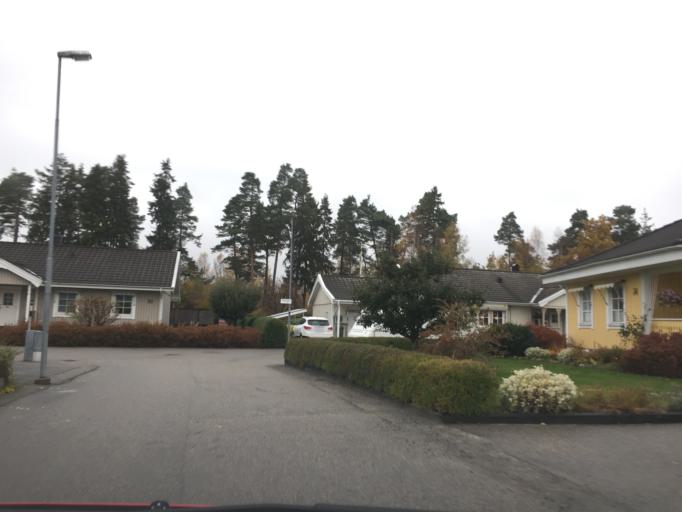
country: SE
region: Vaestra Goetaland
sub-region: Trollhattan
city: Trollhattan
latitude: 58.2314
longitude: 12.3130
